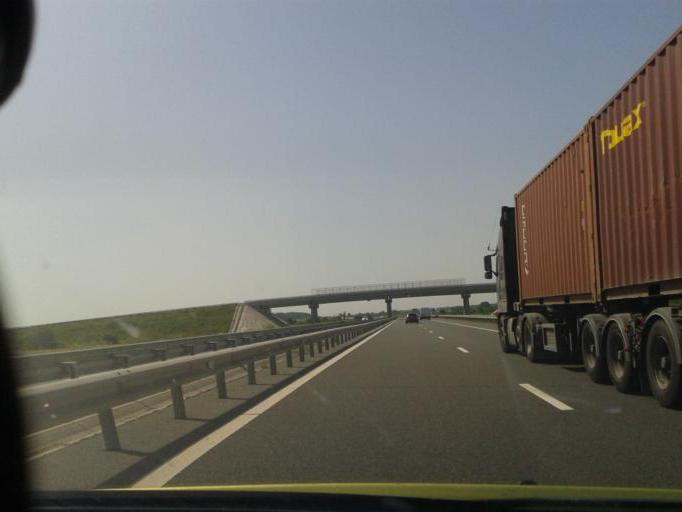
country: RO
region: Prahova
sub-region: Comuna Rafov
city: Rafov
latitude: 44.8785
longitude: 26.1364
